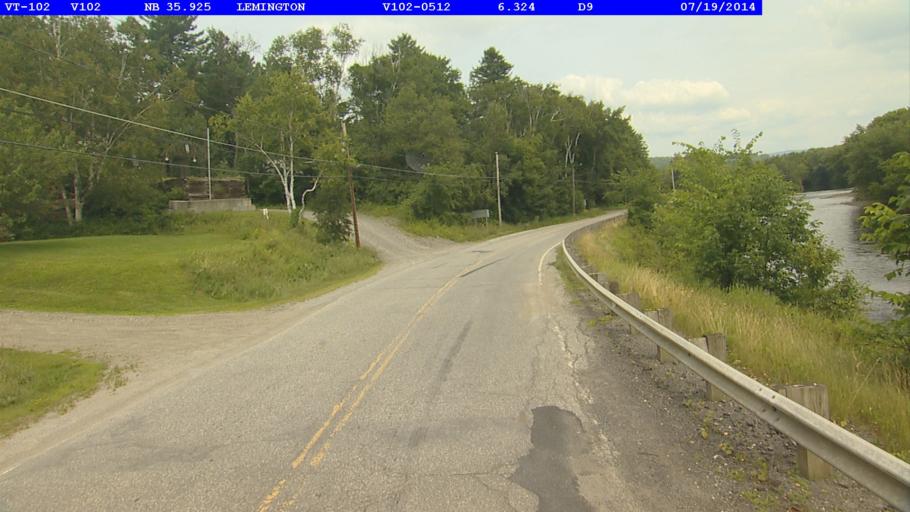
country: US
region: New Hampshire
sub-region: Coos County
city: Colebrook
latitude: 44.8993
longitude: -71.5081
